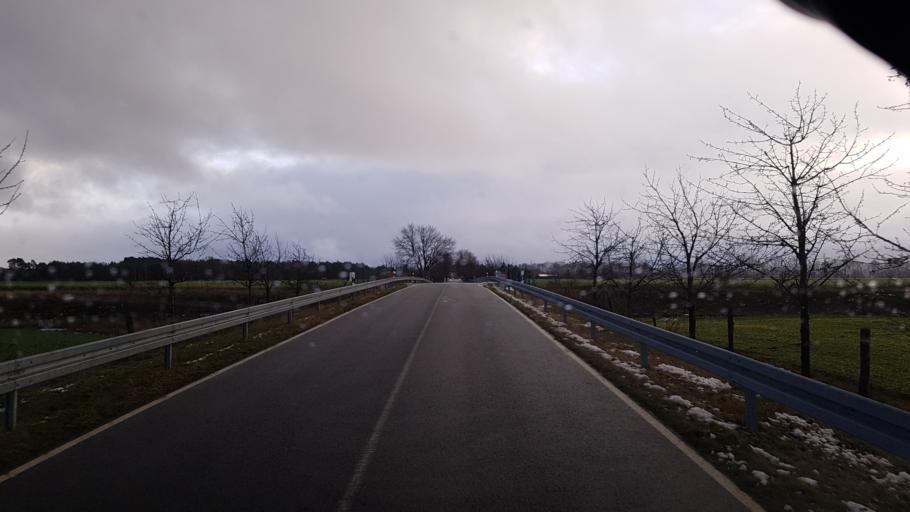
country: DE
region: Brandenburg
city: Heinersbruck
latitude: 51.8300
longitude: 14.5059
